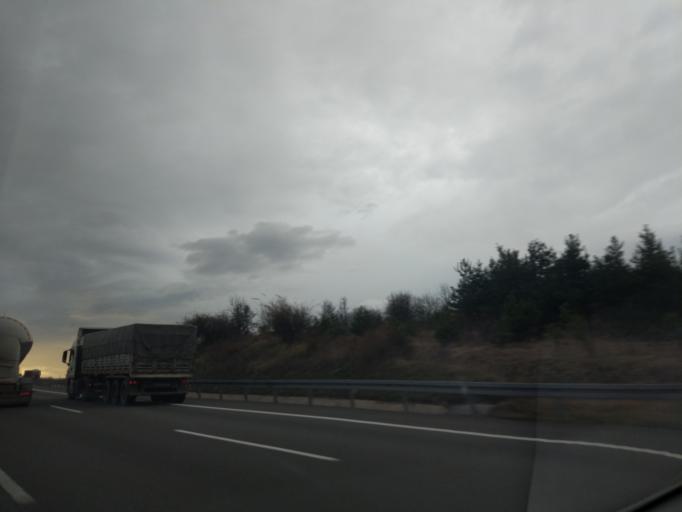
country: TR
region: Bolu
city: Yenicaga
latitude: 40.7540
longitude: 31.9612
